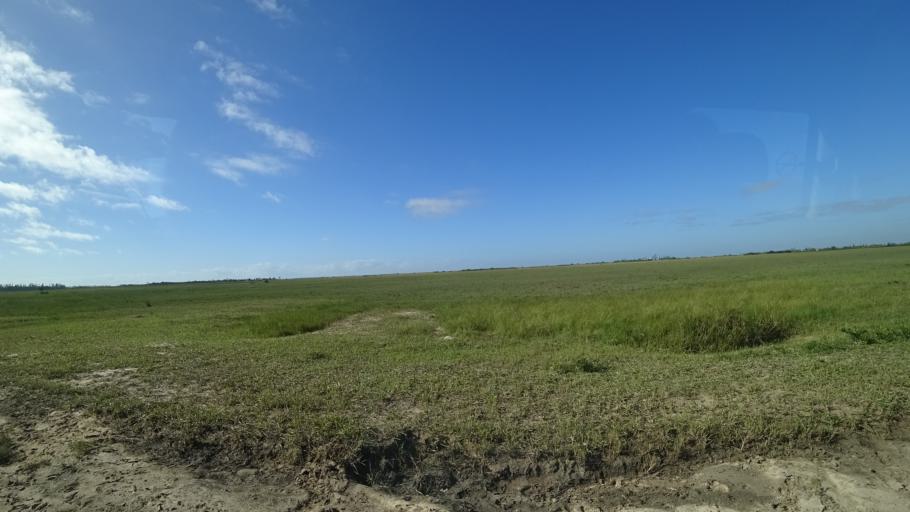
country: MZ
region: Sofala
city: Beira
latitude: -19.7285
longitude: 34.9854
